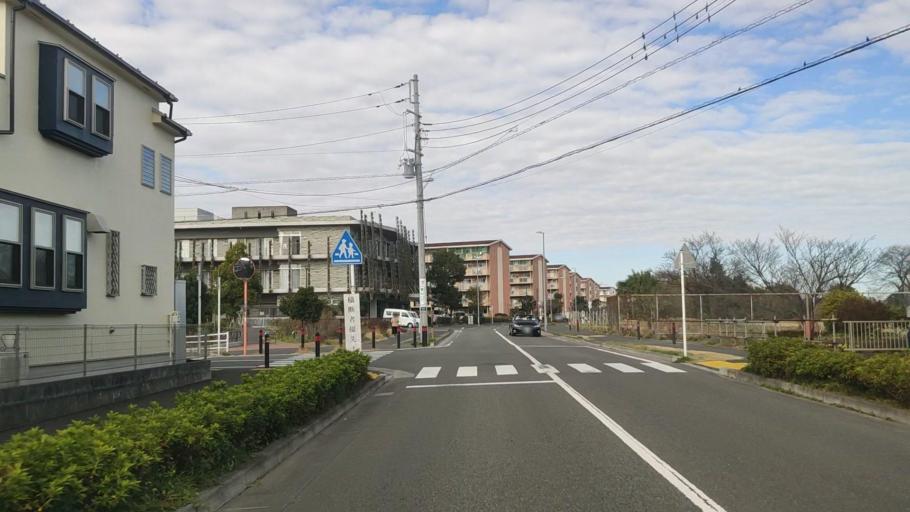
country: JP
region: Kanagawa
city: Minami-rinkan
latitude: 35.4798
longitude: 139.4910
